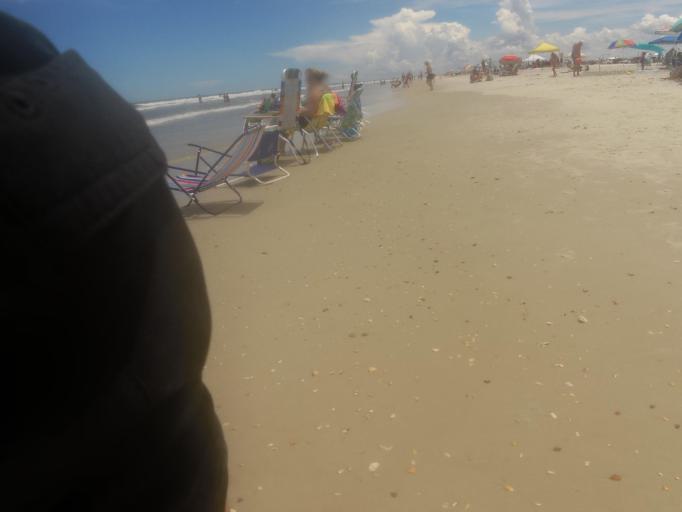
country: US
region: Florida
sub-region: Saint Johns County
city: Saint Augustine Beach
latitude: 29.8355
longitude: -81.2633
